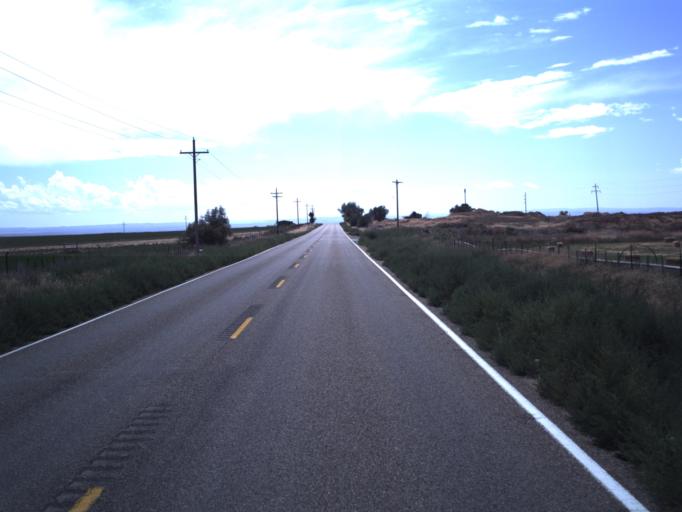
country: US
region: Utah
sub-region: Uintah County
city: Maeser
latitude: 40.2297
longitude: -109.6844
